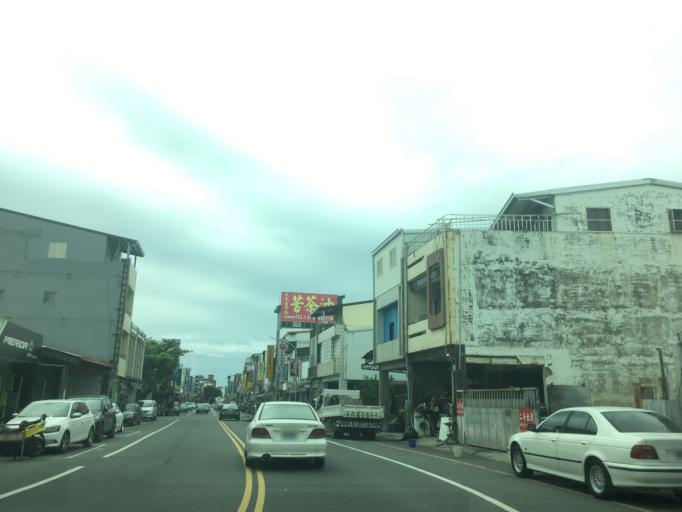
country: TW
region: Taiwan
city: Taitung City
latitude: 22.7594
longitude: 121.1401
